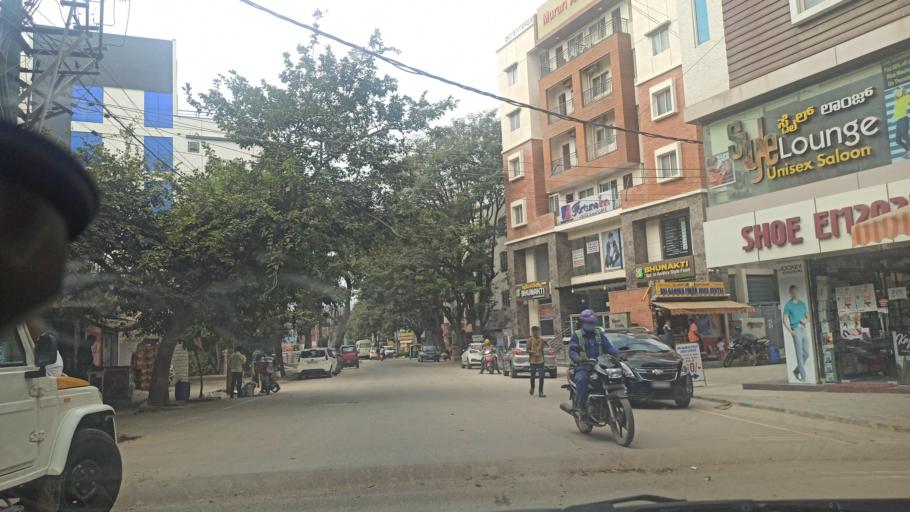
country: IN
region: Karnataka
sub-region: Bangalore Urban
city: Yelahanka
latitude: 13.0398
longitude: 77.6206
